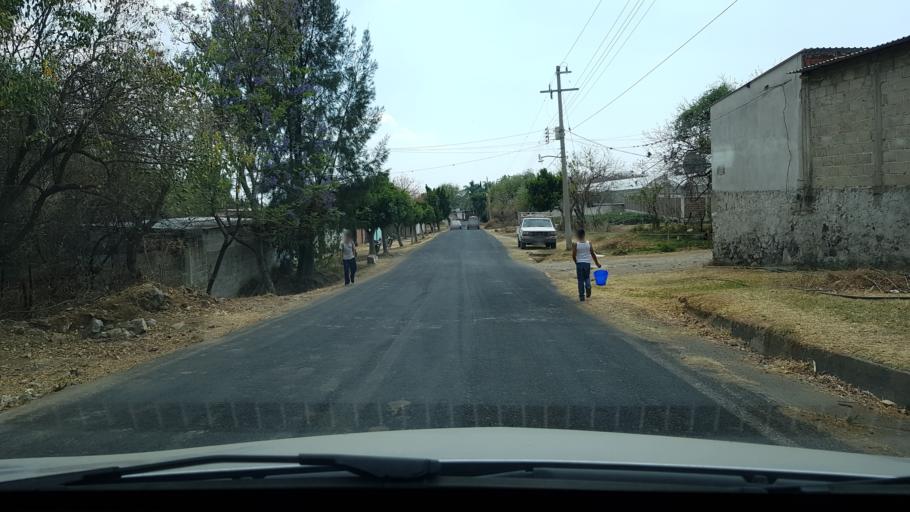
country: MX
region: Morelos
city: Tlacotepec
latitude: 18.8199
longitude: -98.7436
